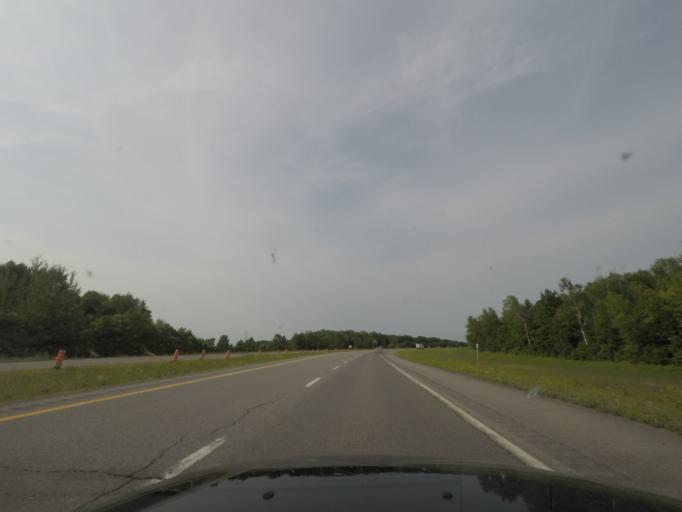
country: CA
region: Quebec
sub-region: Monteregie
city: Napierville
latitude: 45.1621
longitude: -73.4675
